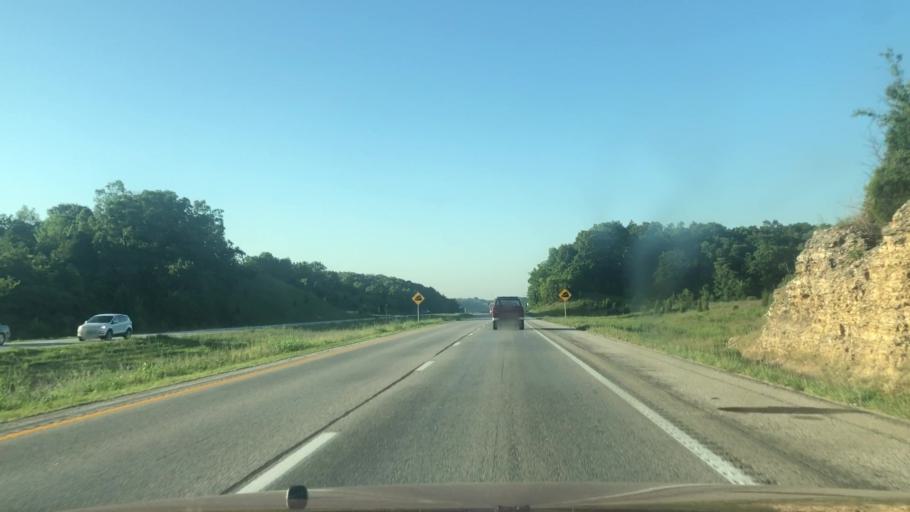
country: US
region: Missouri
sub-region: Christian County
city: Ozark
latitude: 36.8783
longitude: -93.2328
